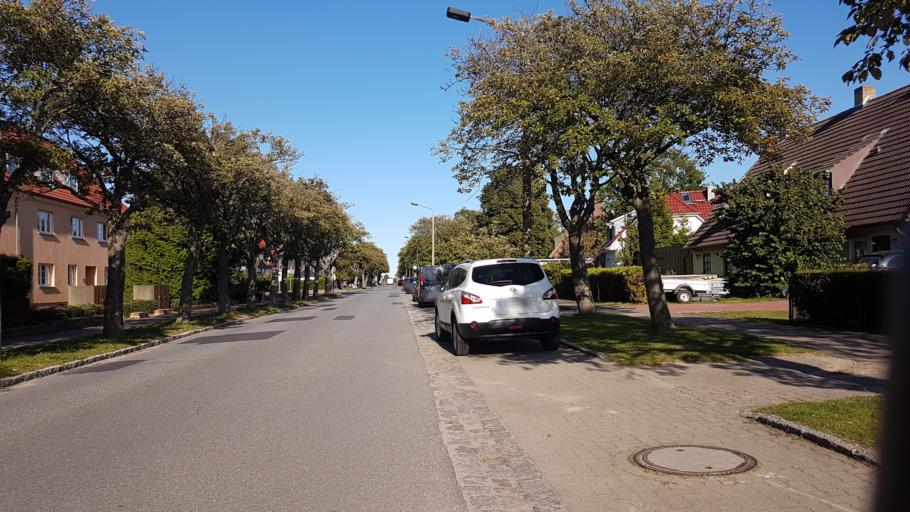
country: DE
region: Mecklenburg-Vorpommern
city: Dranske
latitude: 54.6287
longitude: 13.2299
